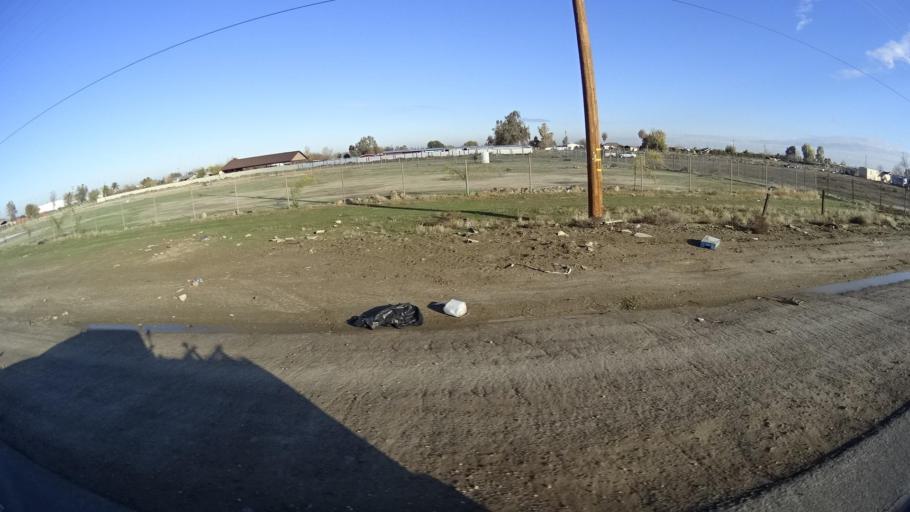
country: US
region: California
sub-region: Kern County
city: Delano
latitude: 35.7758
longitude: -119.3010
